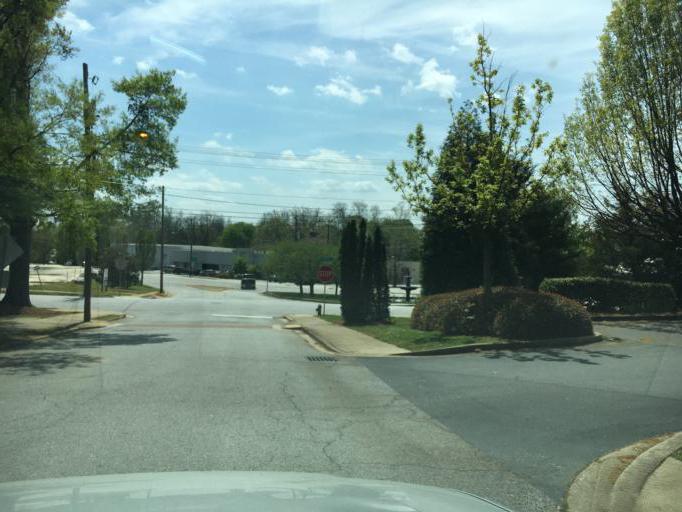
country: US
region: South Carolina
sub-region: Spartanburg County
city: Spartanburg
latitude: 34.9493
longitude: -81.9244
